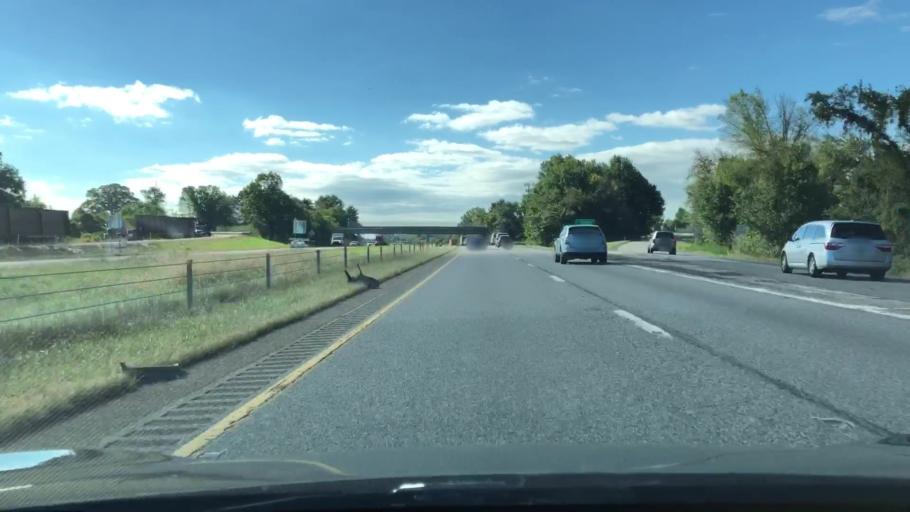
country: US
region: Pennsylvania
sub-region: Bucks County
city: Woodside
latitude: 40.2371
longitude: -74.8818
